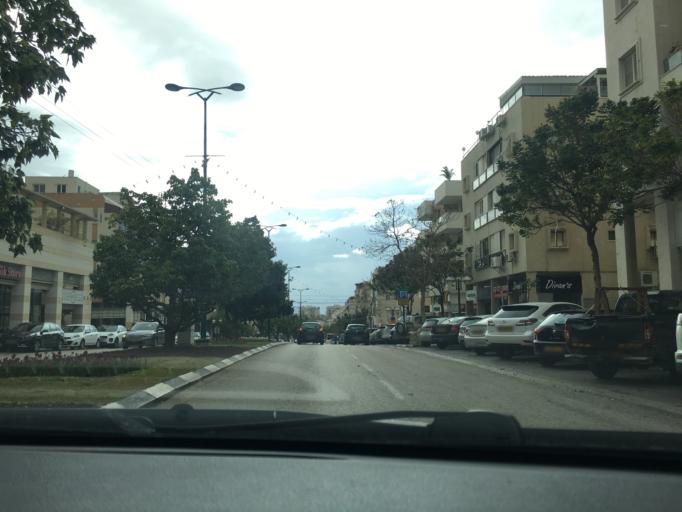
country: IL
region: Tel Aviv
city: Ramat HaSharon
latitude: 32.1433
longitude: 34.8437
